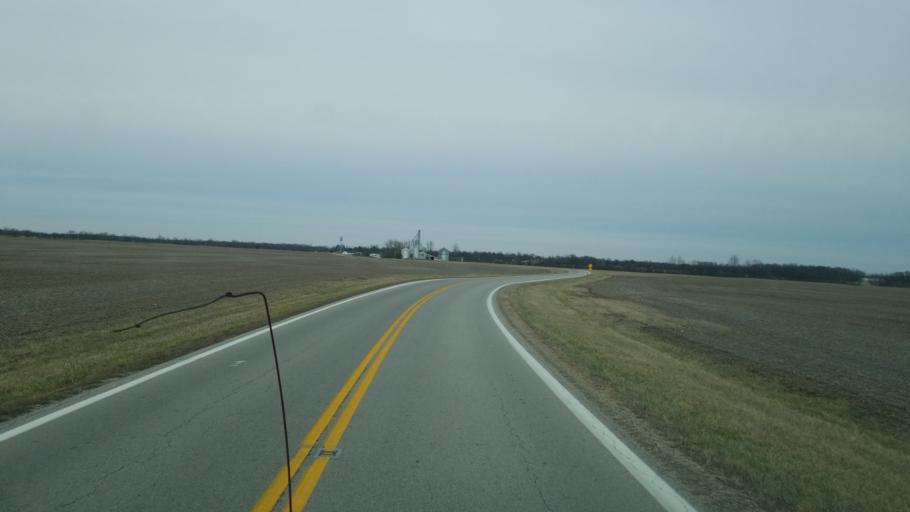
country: US
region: Ohio
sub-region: Ross County
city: Frankfort
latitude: 39.4945
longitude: -83.1696
